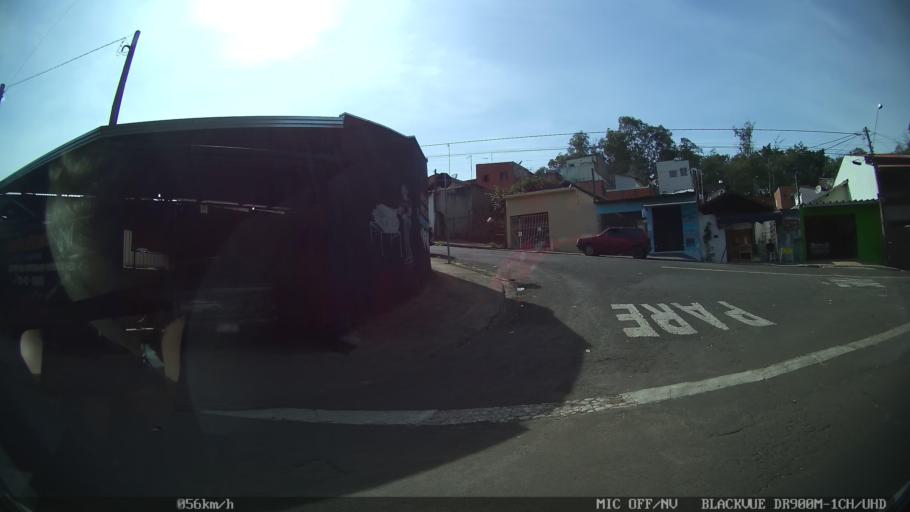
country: BR
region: Sao Paulo
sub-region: Piracicaba
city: Piracicaba
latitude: -22.7607
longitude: -47.6005
